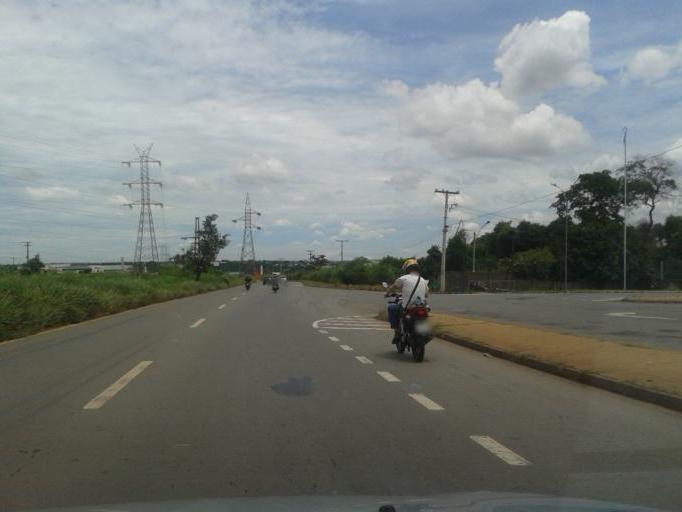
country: BR
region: Goias
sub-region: Aparecida De Goiania
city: Aparecida de Goiania
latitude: -16.7872
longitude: -49.2416
